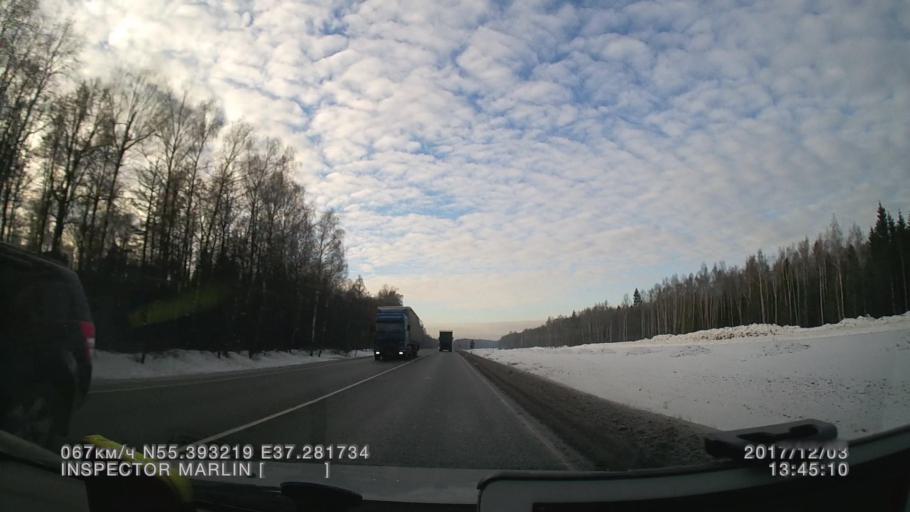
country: RU
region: Moskovskaya
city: Troitsk
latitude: 55.3932
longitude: 37.2821
